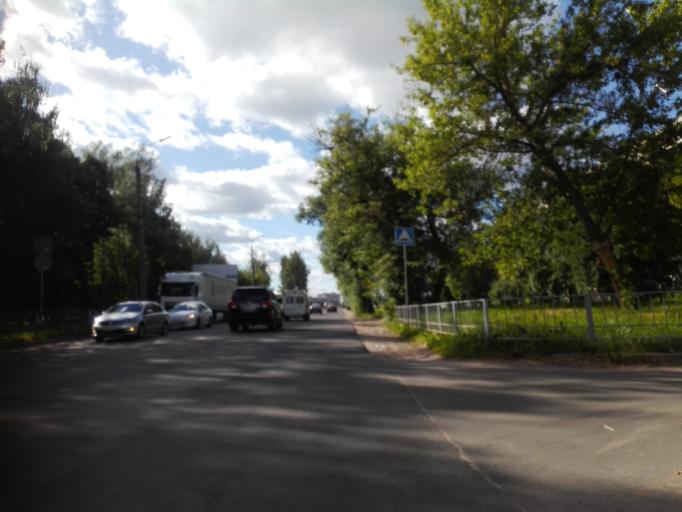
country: RU
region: Orjol
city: Orel
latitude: 52.9364
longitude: 36.0359
